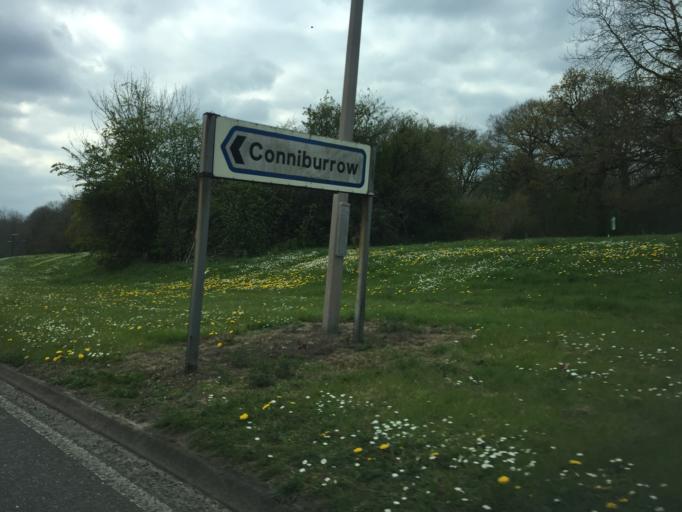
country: GB
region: England
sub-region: Milton Keynes
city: Milton Keynes
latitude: 52.0527
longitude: -0.7616
